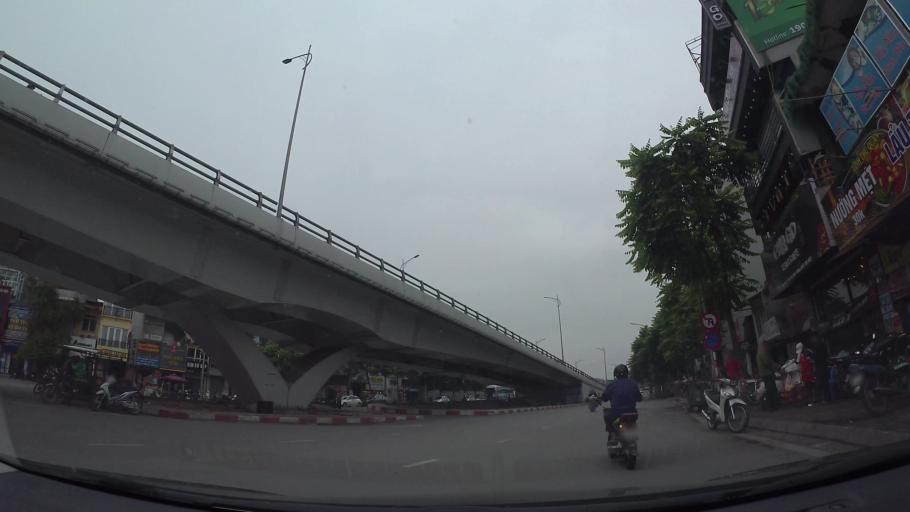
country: VN
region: Ha Noi
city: Hai BaTrung
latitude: 21.0089
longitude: 105.8610
